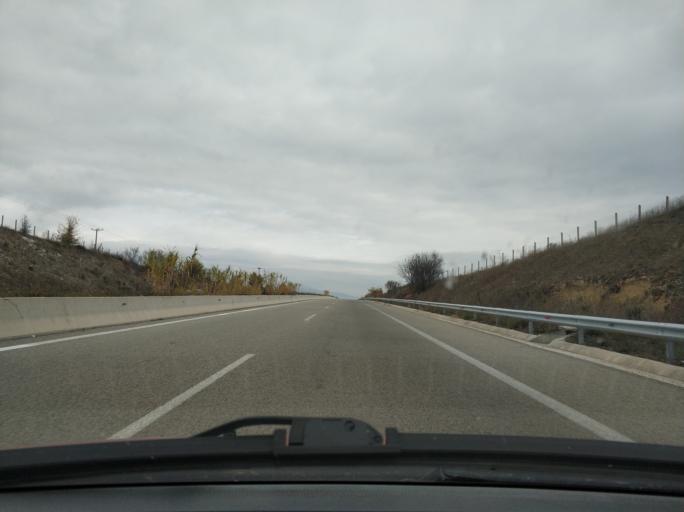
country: GR
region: East Macedonia and Thrace
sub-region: Nomos Kavalas
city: Paralia Ofryniou
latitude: 40.8001
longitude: 24.0177
